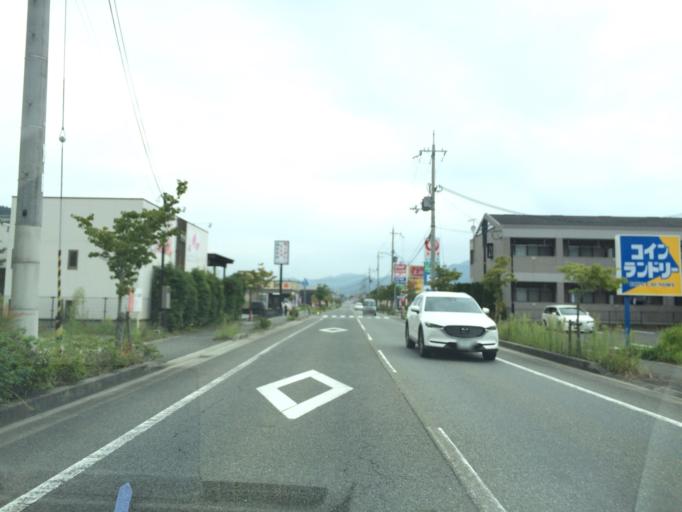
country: JP
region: Hyogo
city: Toyooka
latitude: 35.5378
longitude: 134.8089
